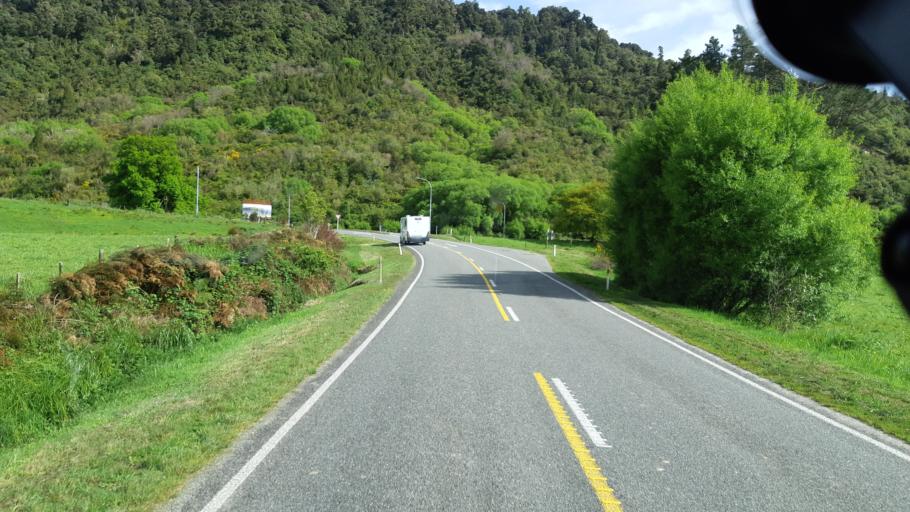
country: NZ
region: West Coast
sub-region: Buller District
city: Westport
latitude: -41.8587
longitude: 171.9383
